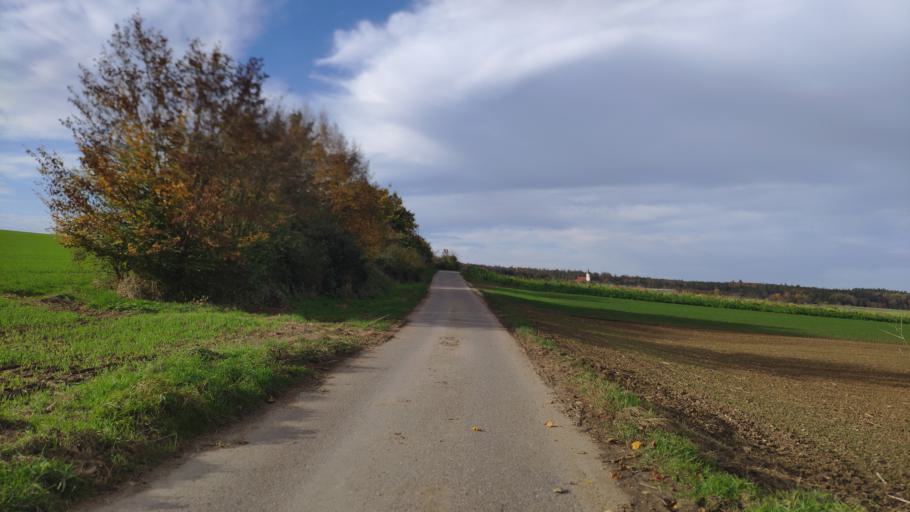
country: DE
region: Baden-Wuerttemberg
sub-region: Tuebingen Region
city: Erbach
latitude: 48.3822
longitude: 9.9195
